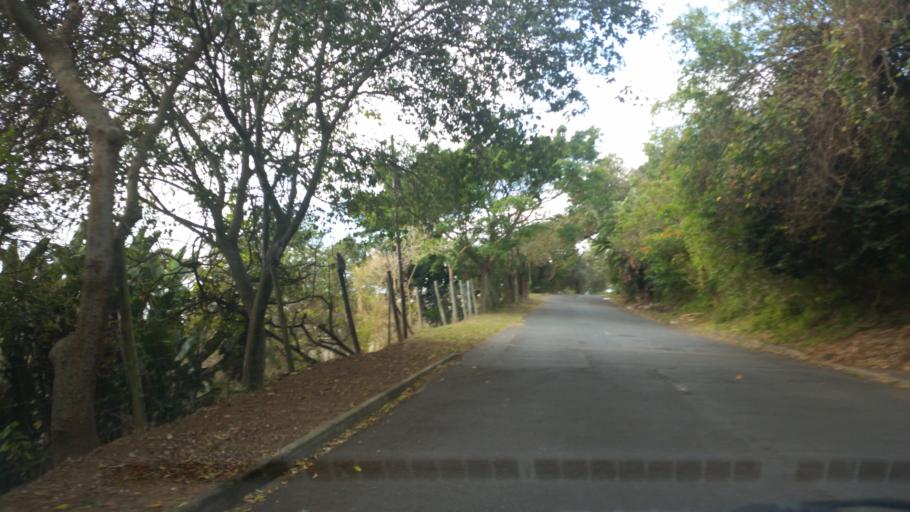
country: ZA
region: KwaZulu-Natal
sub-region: eThekwini Metropolitan Municipality
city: Berea
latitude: -29.8266
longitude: 30.9278
